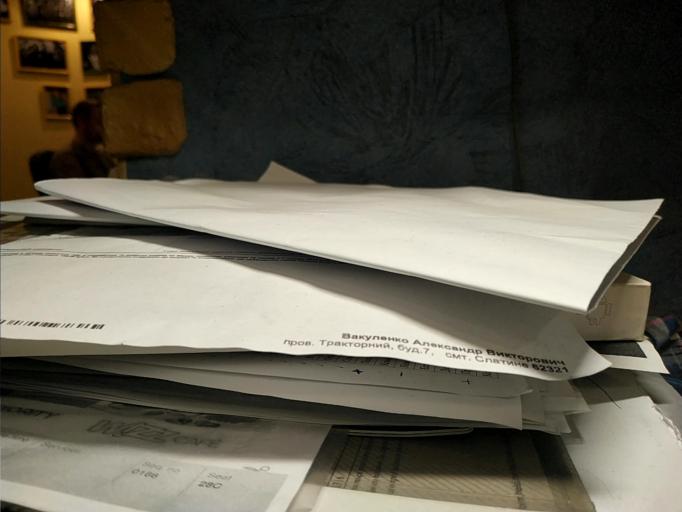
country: RU
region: Tverskaya
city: Zubtsov
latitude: 56.1152
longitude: 34.6016
